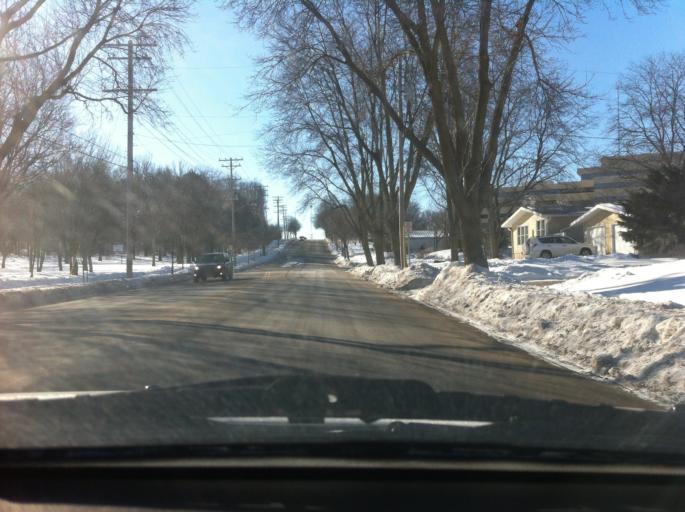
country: US
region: Wisconsin
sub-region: Dane County
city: Shorewood Hills
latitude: 43.0644
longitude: -89.4785
